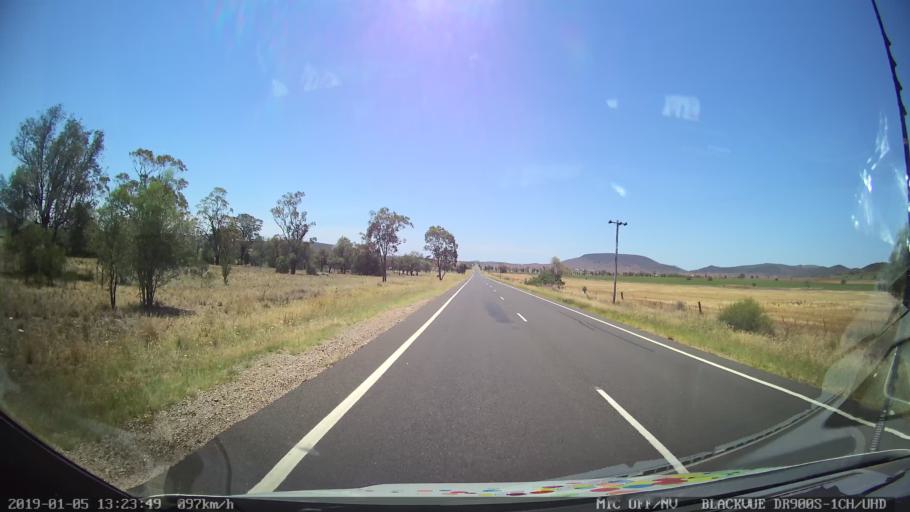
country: AU
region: New South Wales
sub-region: Gunnedah
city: Gunnedah
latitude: -31.0748
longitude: 149.9804
